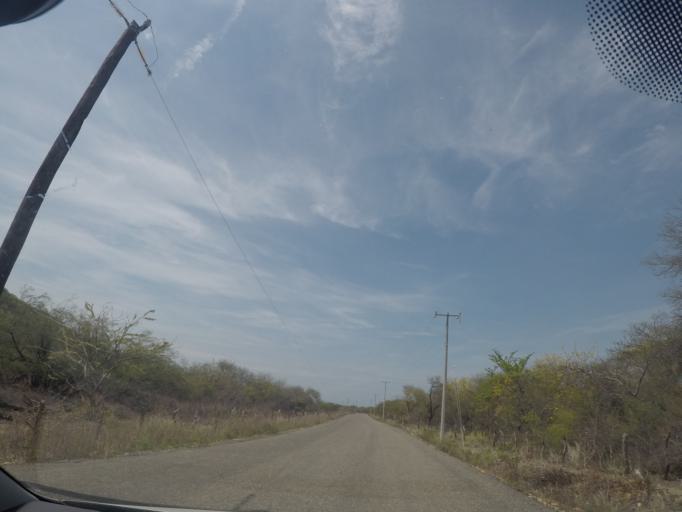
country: MX
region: Oaxaca
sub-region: Salina Cruz
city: Salina Cruz
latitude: 16.2074
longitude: -95.1217
